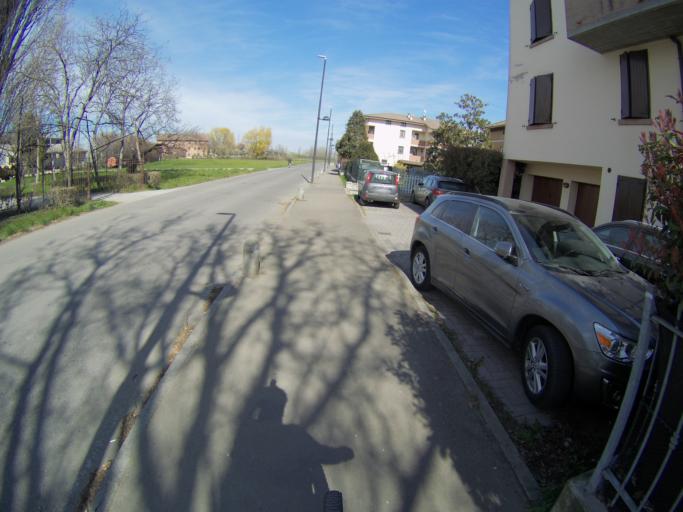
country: IT
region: Emilia-Romagna
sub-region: Provincia di Reggio Emilia
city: Massenzatico
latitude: 44.7117
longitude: 10.6891
